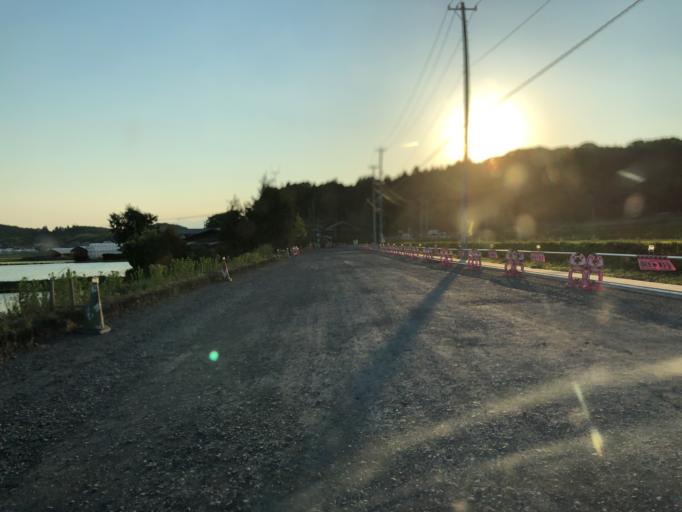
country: JP
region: Fukushima
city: Sukagawa
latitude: 37.1829
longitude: 140.3202
